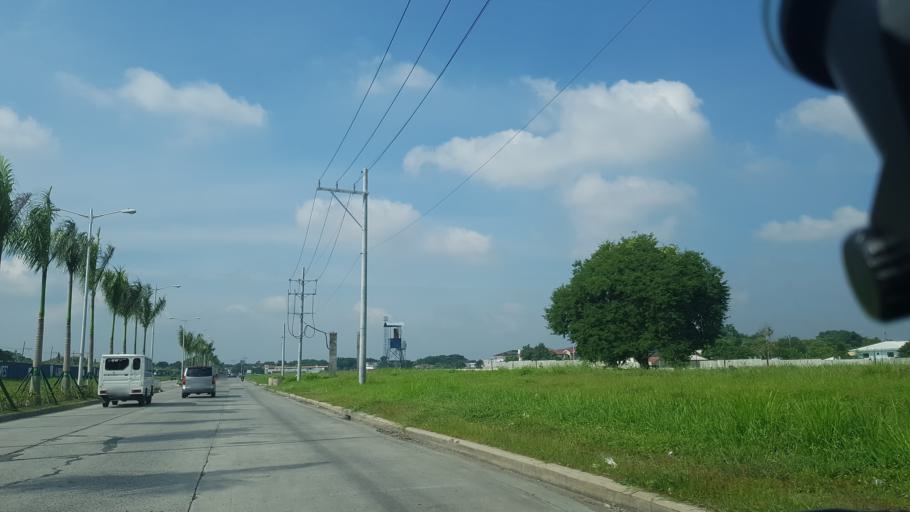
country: PH
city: Sambayanihan People's Village
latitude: 14.4111
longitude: 121.0146
